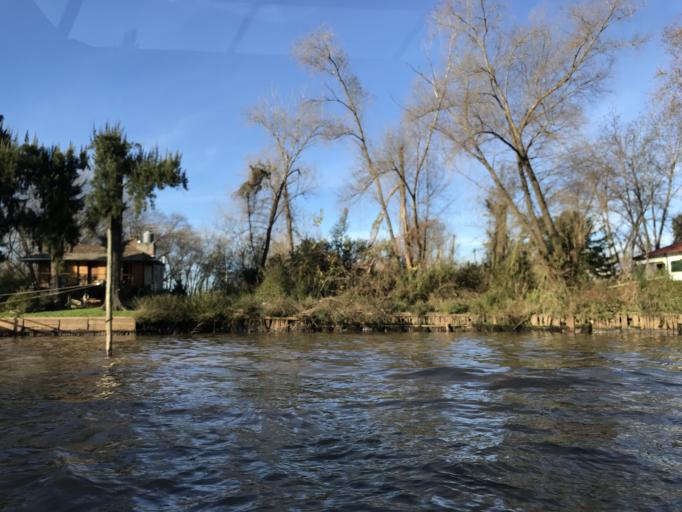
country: AR
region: Buenos Aires
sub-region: Partido de Tigre
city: Tigre
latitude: -34.4033
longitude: -58.5940
